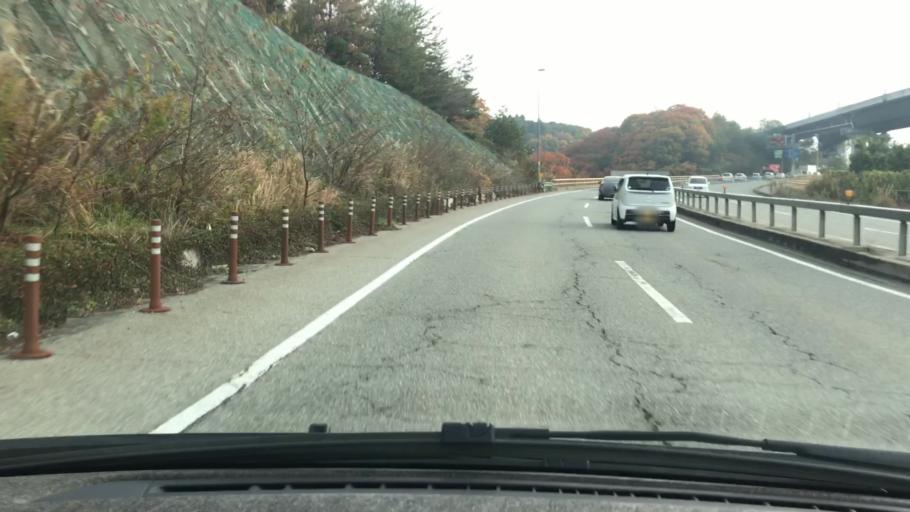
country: JP
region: Hyogo
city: Sandacho
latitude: 34.8340
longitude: 135.2578
